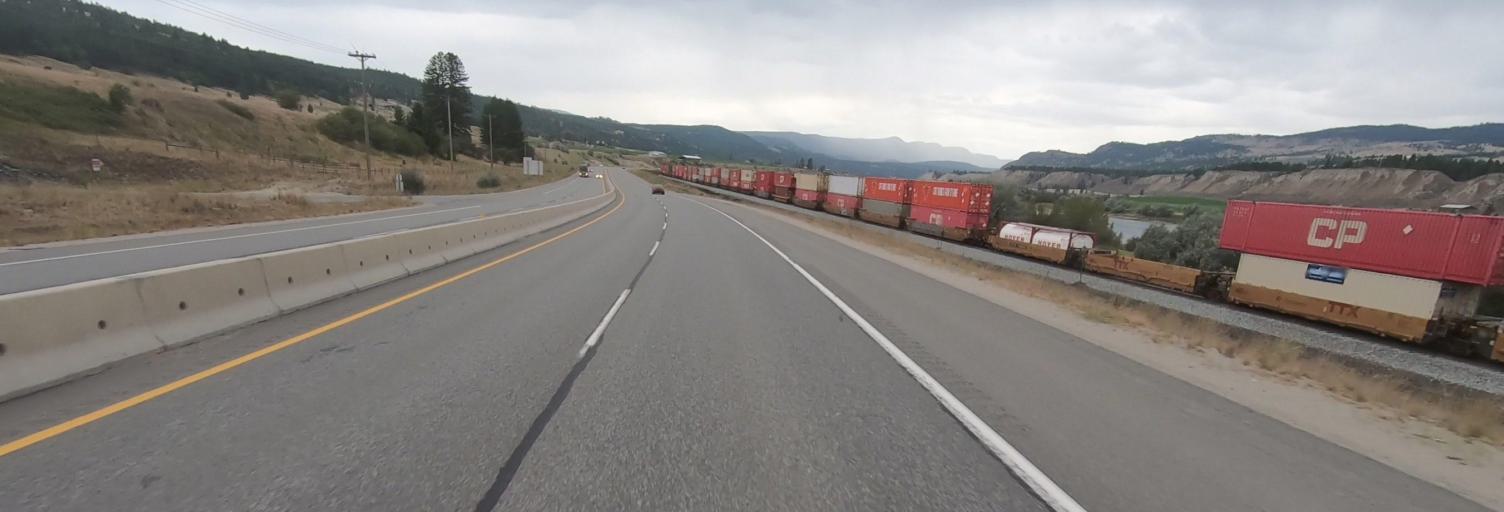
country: CA
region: British Columbia
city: Chase
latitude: 50.6799
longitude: -119.8275
